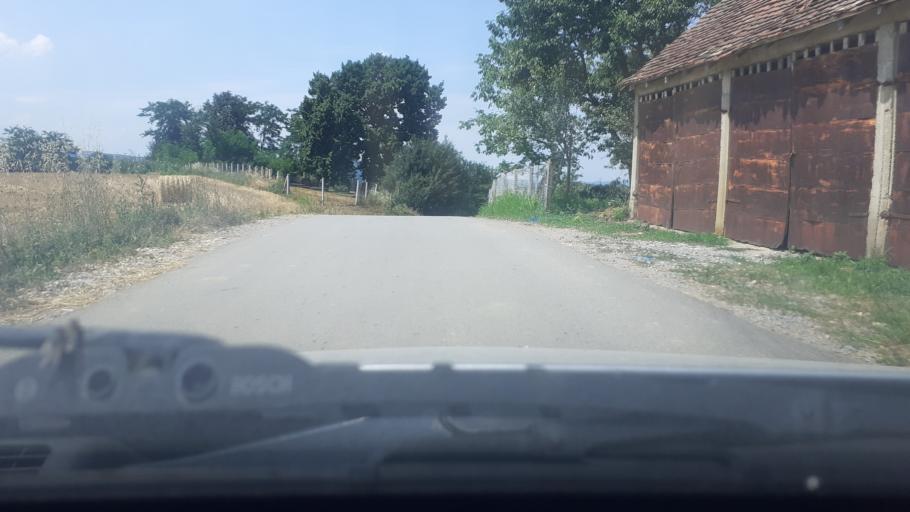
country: RS
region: Central Serbia
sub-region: Kolubarski Okrug
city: Osecina
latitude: 44.3900
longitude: 19.5013
